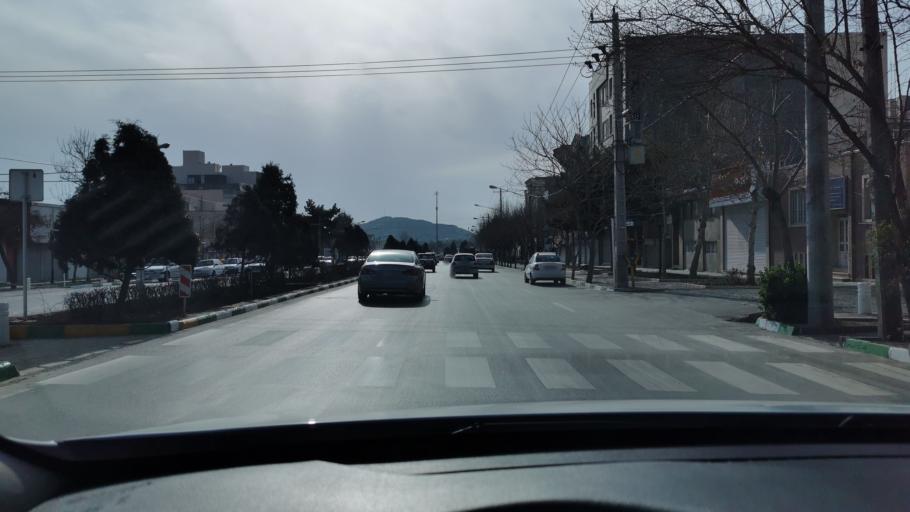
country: IR
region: Razavi Khorasan
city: Mashhad
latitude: 36.2857
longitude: 59.5466
